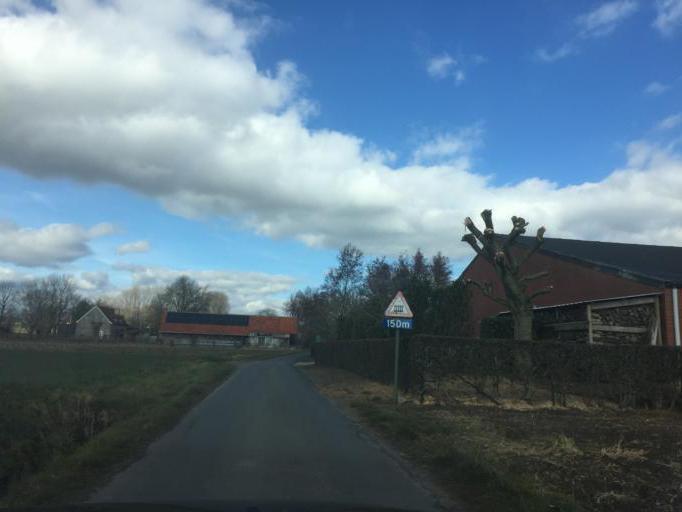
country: BE
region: Flanders
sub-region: Provincie West-Vlaanderen
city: Lichtervelde
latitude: 50.9941
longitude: 3.1587
